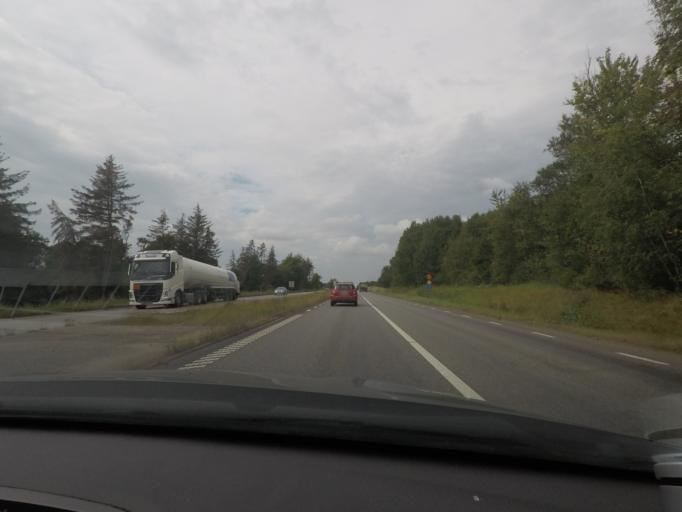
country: SE
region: Halland
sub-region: Halmstads Kommun
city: Fyllinge
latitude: 56.6416
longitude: 12.9222
